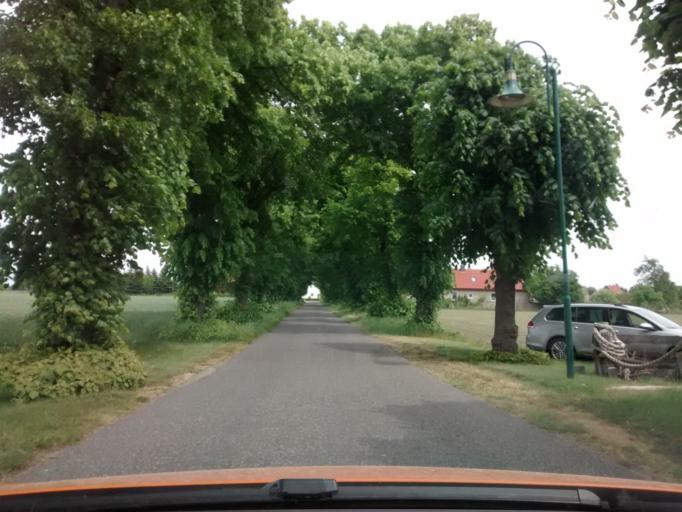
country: DE
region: Saxony-Anhalt
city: Holzdorf
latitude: 51.8408
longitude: 13.2105
